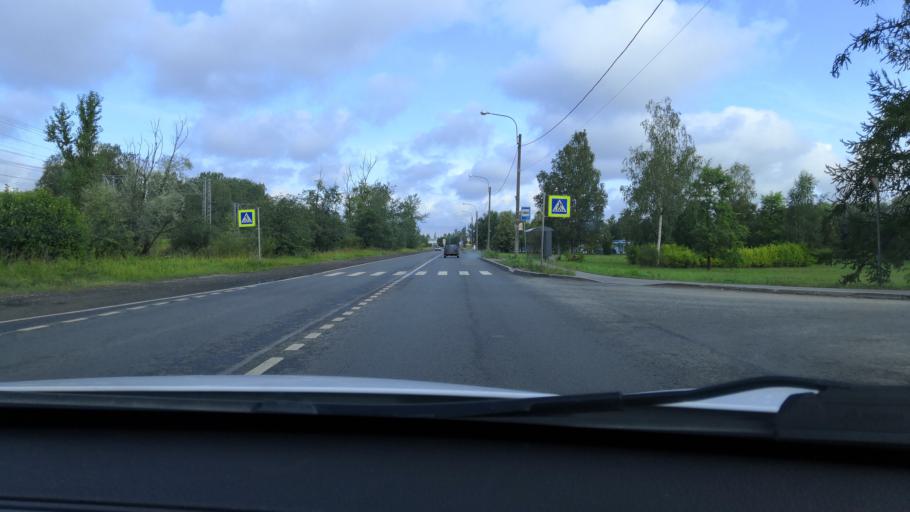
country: RU
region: St.-Petersburg
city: Tyarlevo
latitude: 59.7083
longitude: 30.4374
